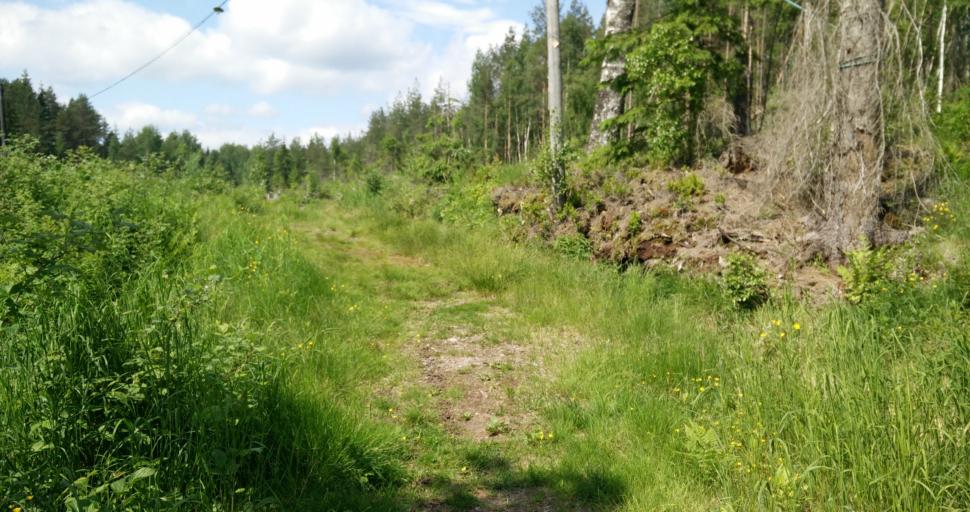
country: SE
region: Vaermland
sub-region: Hagfors Kommun
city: Hagfors
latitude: 60.0109
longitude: 13.5790
